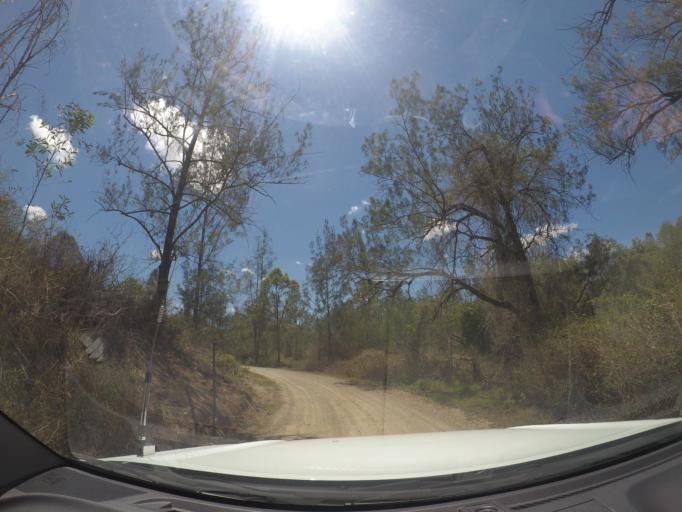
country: AU
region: Queensland
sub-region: Ipswich
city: Springfield Lakes
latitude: -27.8189
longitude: 152.8464
